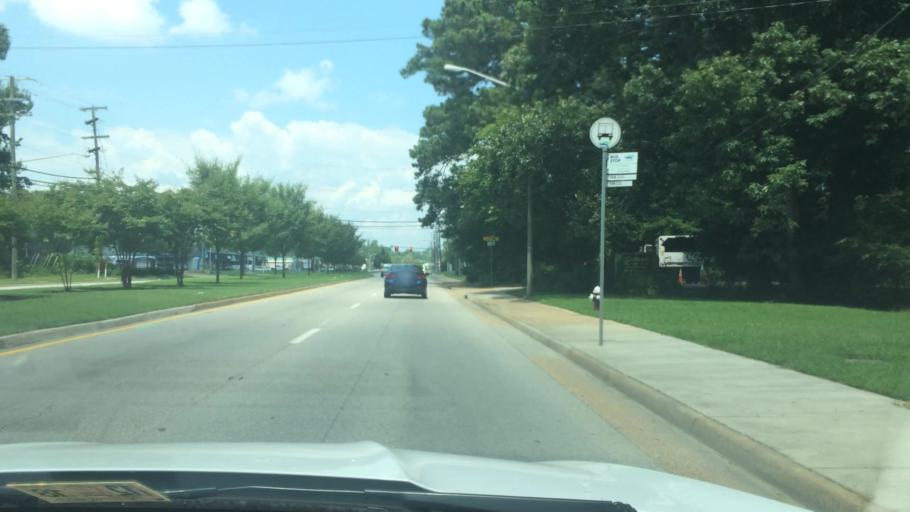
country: US
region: Virginia
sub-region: York County
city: Yorktown
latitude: 37.1545
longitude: -76.5551
